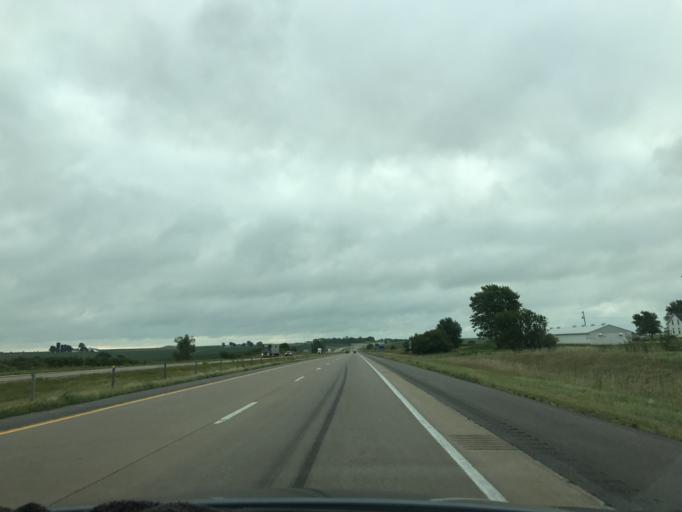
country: US
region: Iowa
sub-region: Cedar County
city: Durant
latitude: 41.6339
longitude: -90.9414
